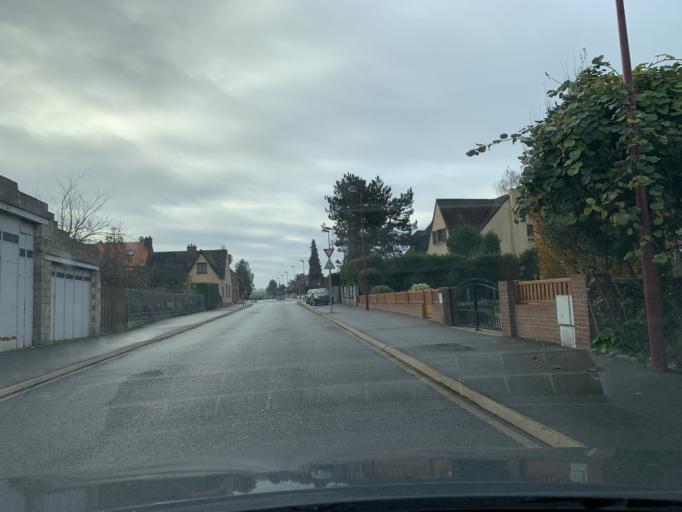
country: FR
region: Nord-Pas-de-Calais
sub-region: Departement du Nord
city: Neuville-Saint-Remy
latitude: 50.1871
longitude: 3.2168
